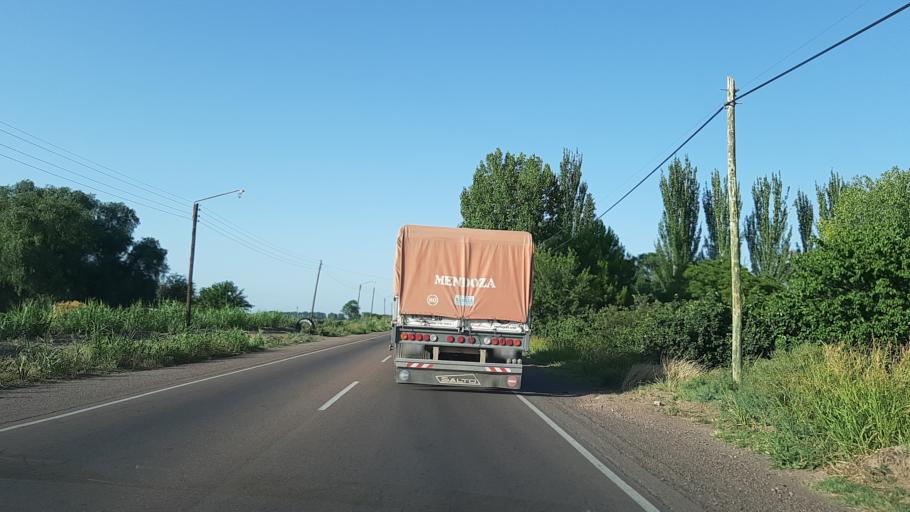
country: AR
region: Mendoza
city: San Martin
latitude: -32.9897
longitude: -68.4687
